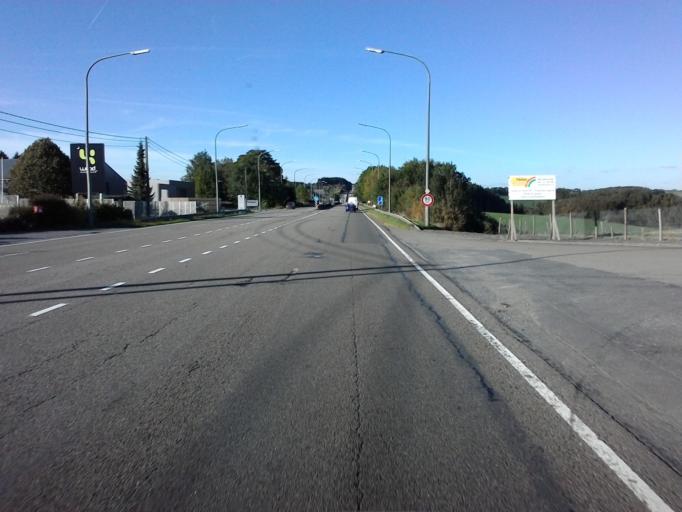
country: BE
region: Wallonia
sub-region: Province du Luxembourg
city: Fauvillers
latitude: 49.8996
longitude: 5.7001
